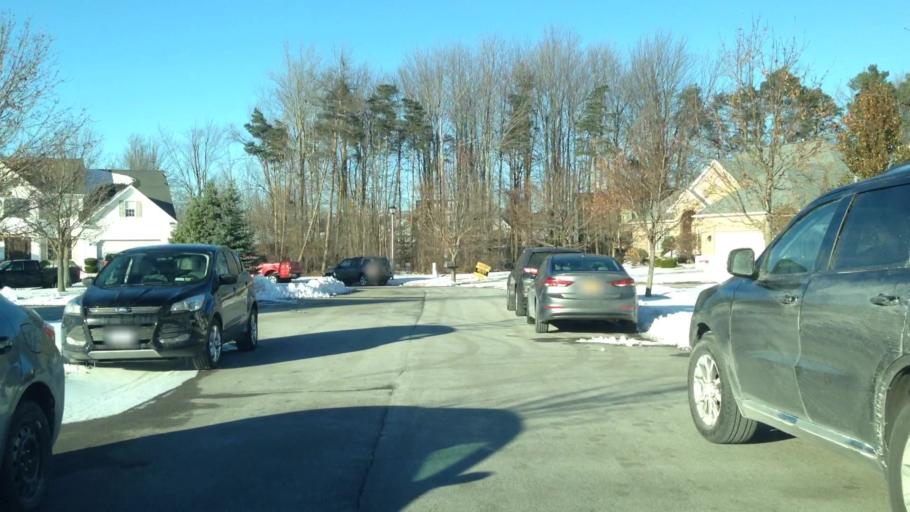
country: US
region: New York
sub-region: Erie County
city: Lancaster
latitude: 42.8670
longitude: -78.6844
